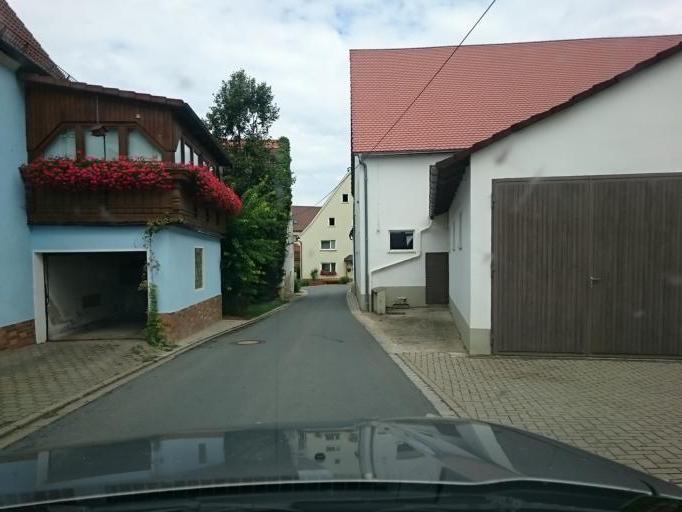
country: DE
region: Bavaria
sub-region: Regierungsbezirk Mittelfranken
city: Hartenstein
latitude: 49.5802
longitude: 11.5394
